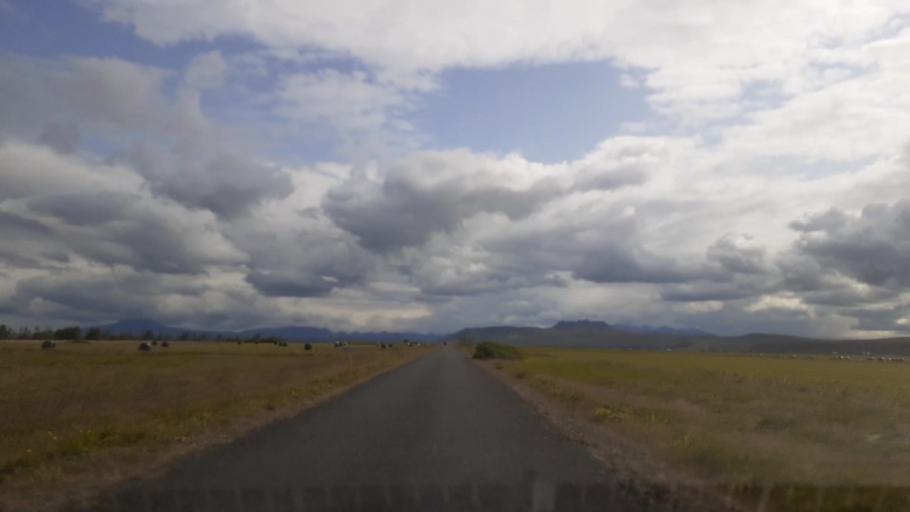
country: IS
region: South
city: Vestmannaeyjar
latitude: 63.7706
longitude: -20.2882
